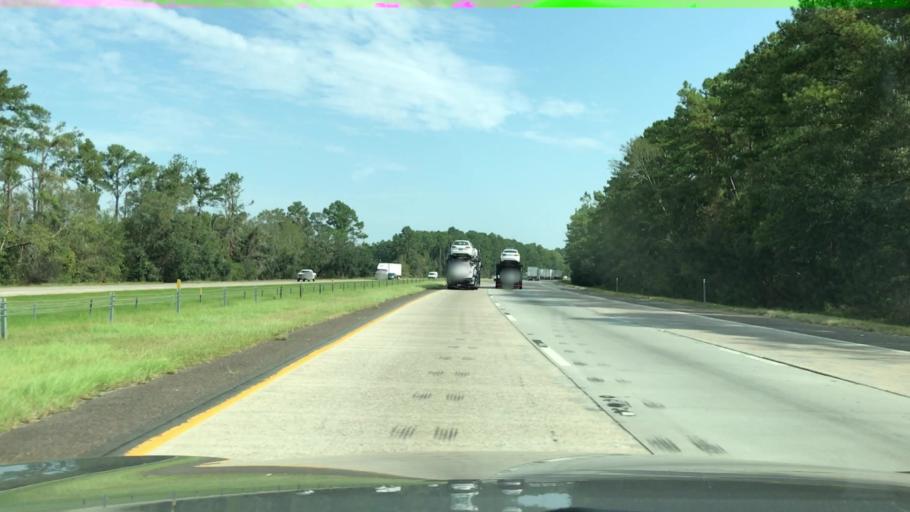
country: US
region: South Carolina
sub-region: Hampton County
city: Yemassee
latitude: 32.8058
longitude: -80.7693
